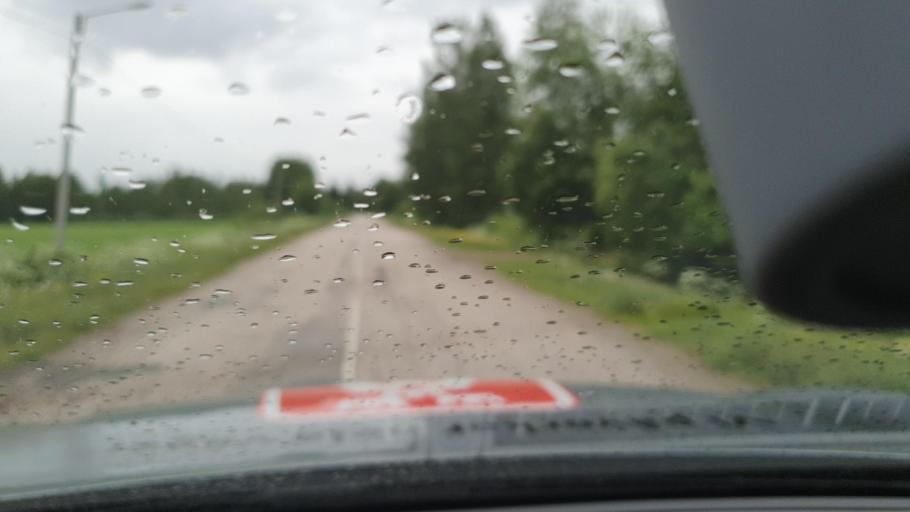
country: SE
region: Norrbotten
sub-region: Overkalix Kommun
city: OEverkalix
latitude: 66.4777
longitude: 22.7770
